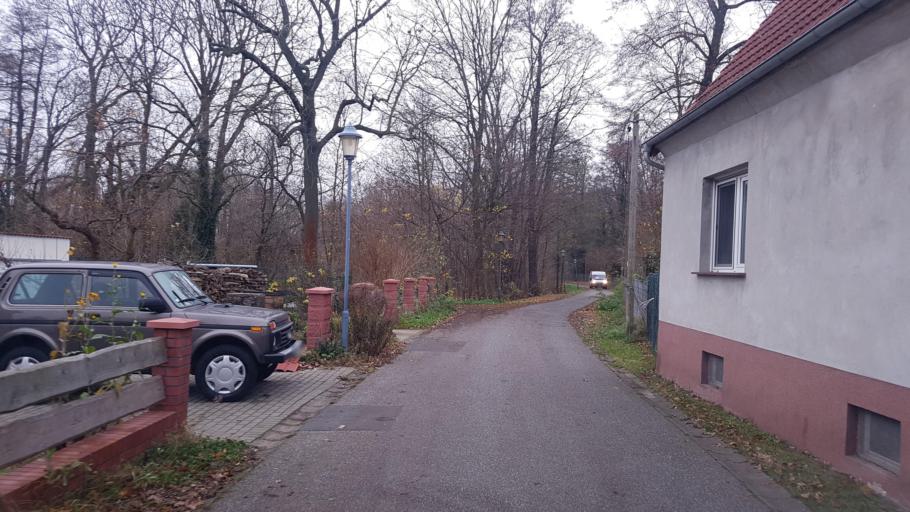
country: DE
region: Brandenburg
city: Lauchhammer
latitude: 51.4669
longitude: 13.7450
